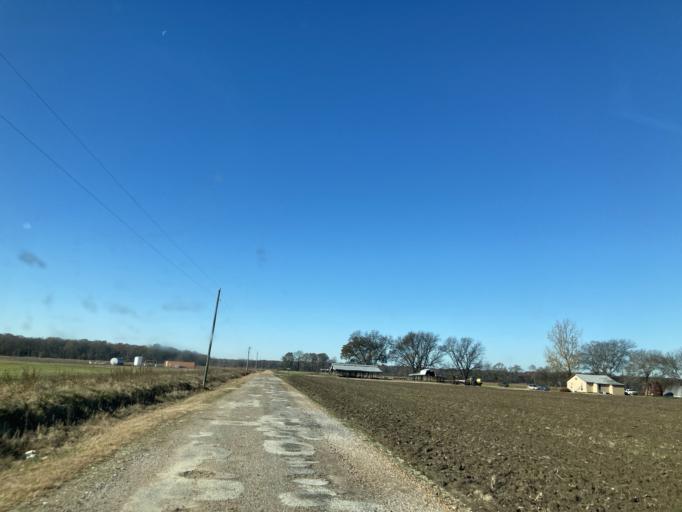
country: US
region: Mississippi
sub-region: Sharkey County
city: Rolling Fork
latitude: 32.8574
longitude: -90.7083
